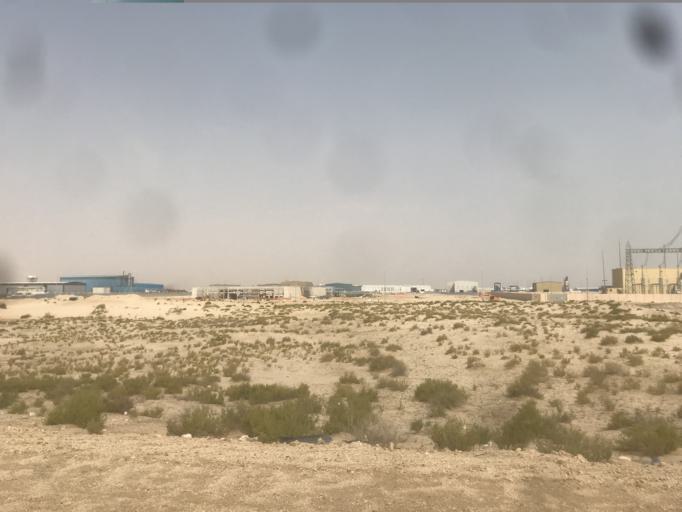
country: SA
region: Eastern Province
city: Abqaiq
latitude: 25.9108
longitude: 49.9594
